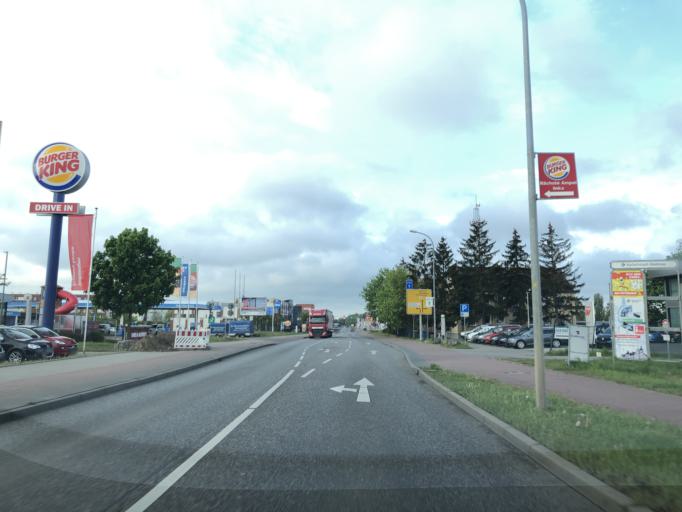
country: DE
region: Mecklenburg-Vorpommern
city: Guestrow
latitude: 53.8109
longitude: 12.1902
